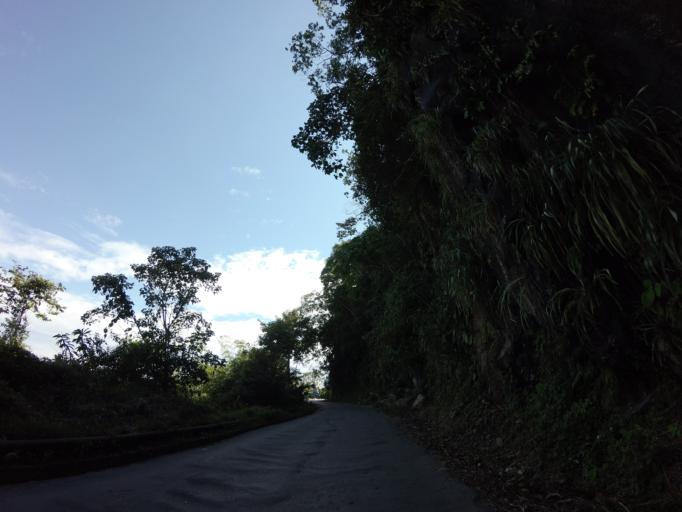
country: CO
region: Caldas
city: Norcasia
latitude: 5.5727
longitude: -74.9019
